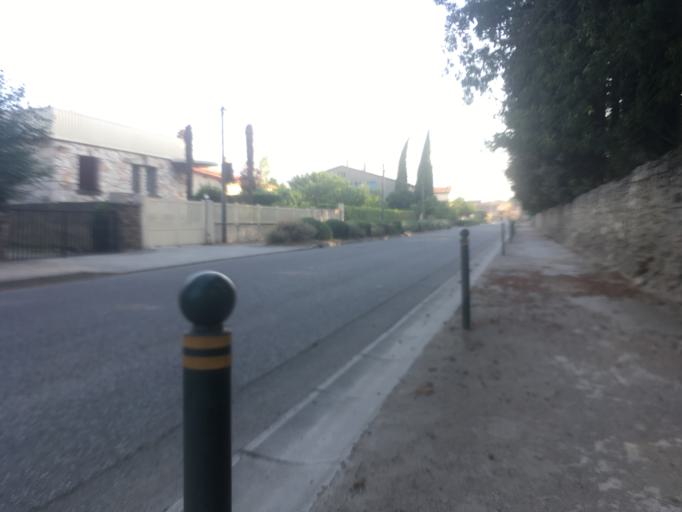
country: FR
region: Languedoc-Roussillon
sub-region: Departement de l'Aude
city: Bram
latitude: 43.2468
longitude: 2.1173
